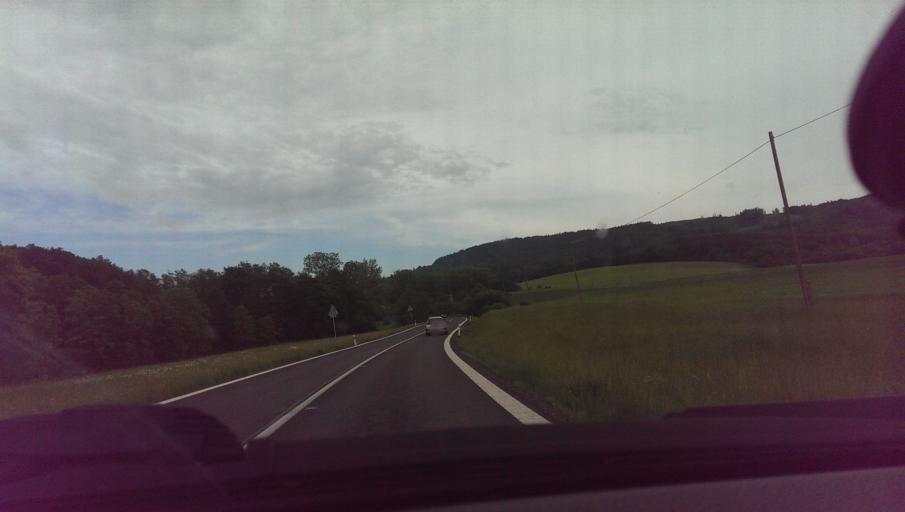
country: CZ
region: Zlin
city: Ujezd
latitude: 49.2270
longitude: 17.9290
